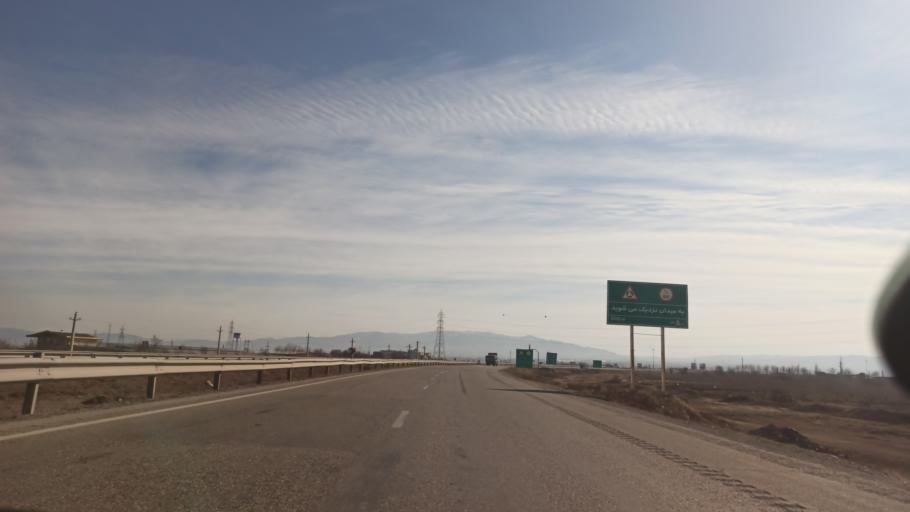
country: IR
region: Qazvin
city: Bu'in Zahra
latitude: 35.7747
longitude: 50.0849
